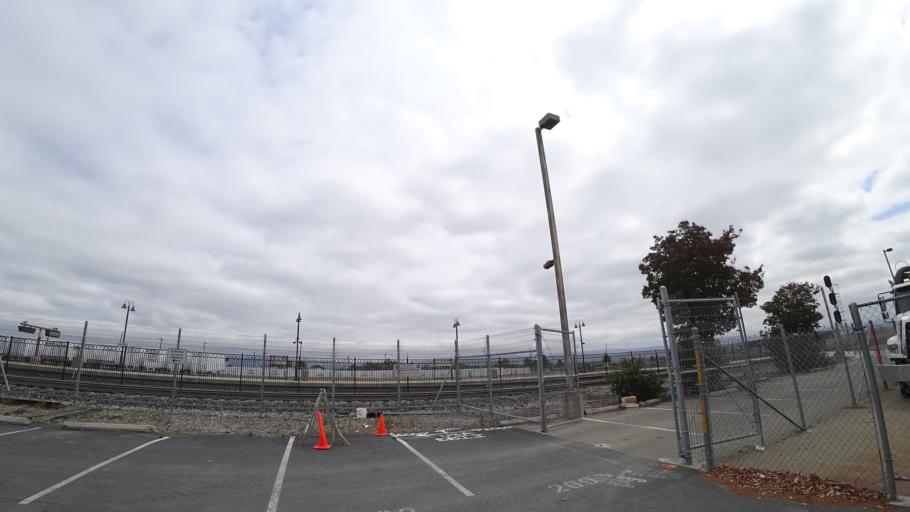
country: US
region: California
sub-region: Santa Clara County
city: Santa Clara
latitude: 37.3524
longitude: -121.9350
